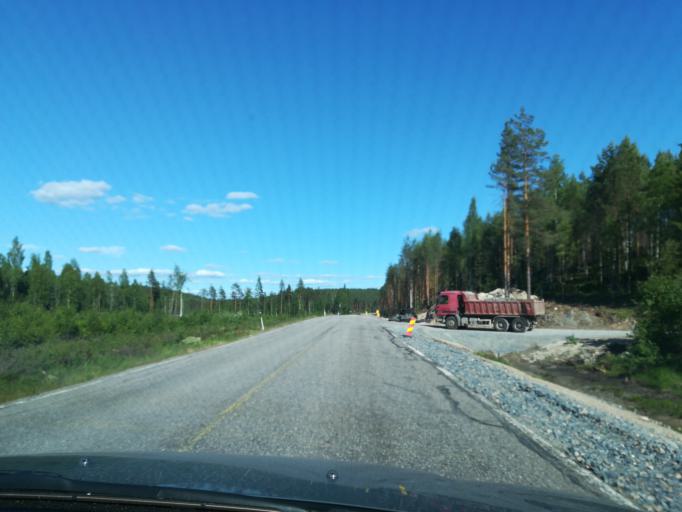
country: FI
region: Southern Savonia
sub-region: Mikkeli
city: Puumala
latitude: 61.4646
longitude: 28.3813
